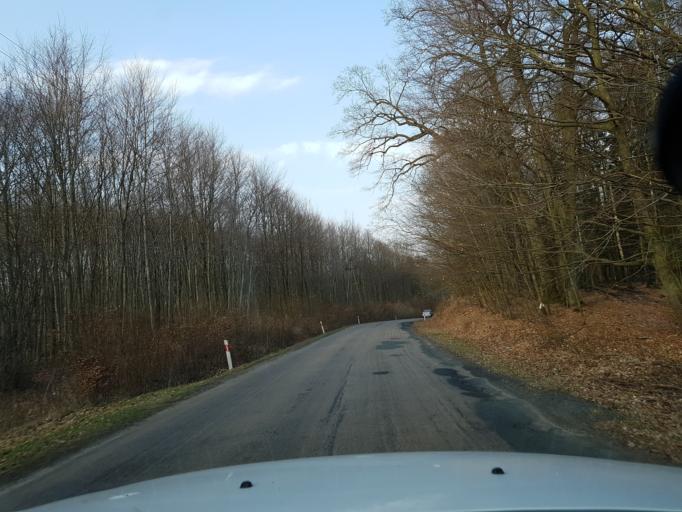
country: PL
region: West Pomeranian Voivodeship
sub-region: Powiat swidwinski
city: Polczyn-Zdroj
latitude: 53.7357
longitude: 16.0760
